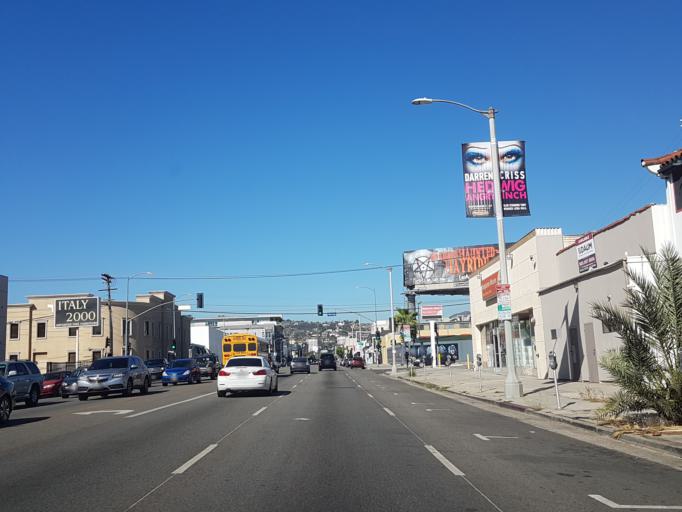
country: US
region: California
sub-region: Los Angeles County
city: West Hollywood
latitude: 34.0846
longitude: -118.3440
